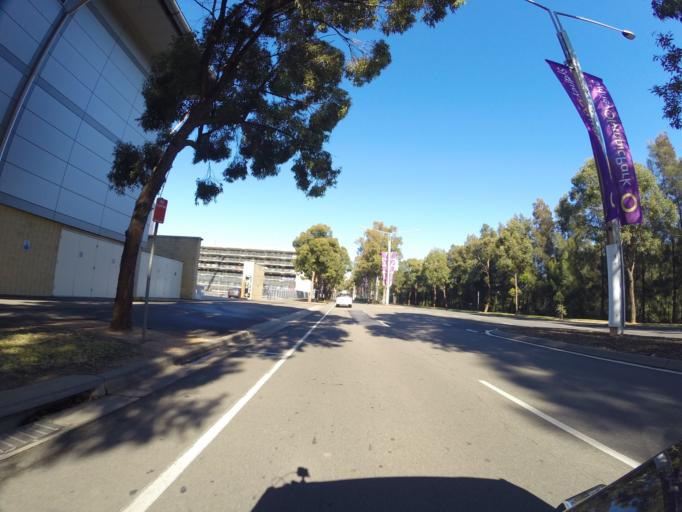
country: AU
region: New South Wales
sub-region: Canada Bay
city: Concord West
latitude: -33.8438
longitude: 151.0611
